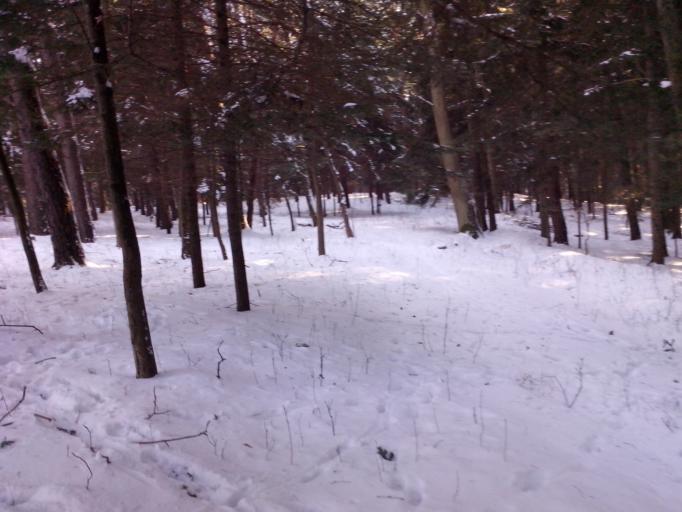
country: PL
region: Subcarpathian Voivodeship
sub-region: Powiat strzyzowski
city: Strzyzow
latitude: 49.8310
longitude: 21.8000
